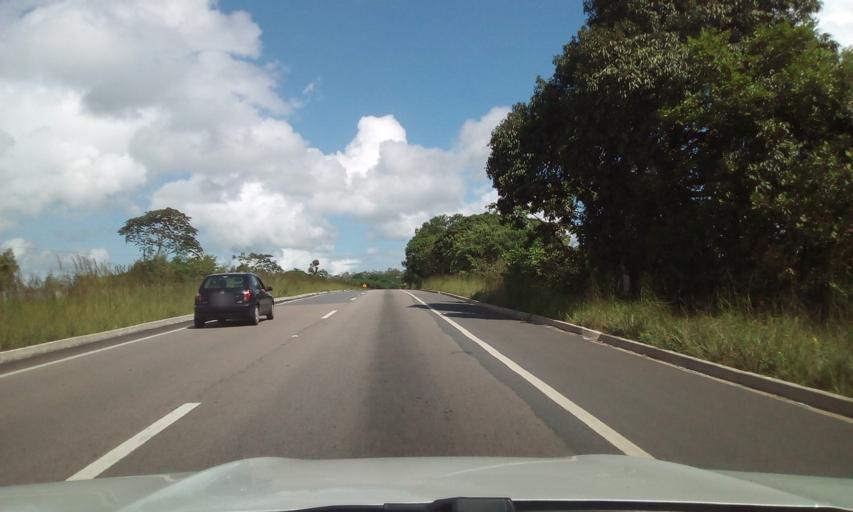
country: BR
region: Paraiba
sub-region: Conde
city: Conde
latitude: -7.2928
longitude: -34.9379
